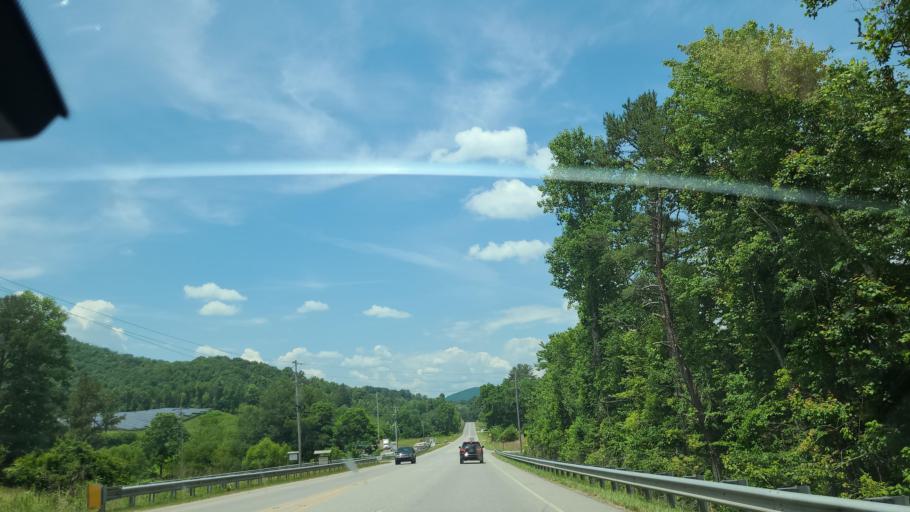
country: US
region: North Carolina
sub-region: Clay County
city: Hayesville
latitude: 35.0374
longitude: -83.8717
